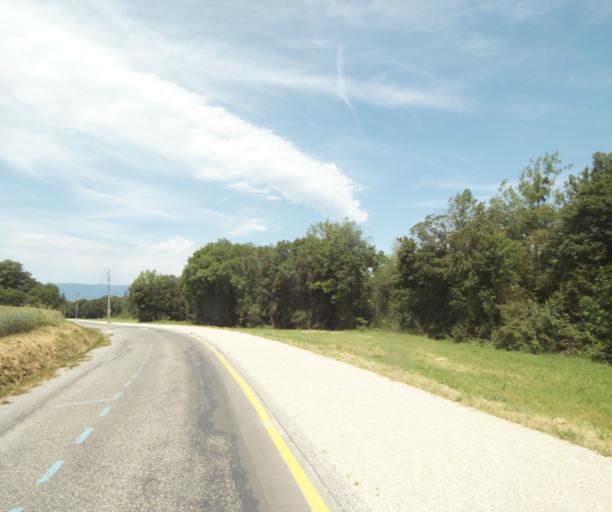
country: FR
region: Rhone-Alpes
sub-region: Departement de la Haute-Savoie
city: Chens-sur-Leman
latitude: 46.3182
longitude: 6.2658
